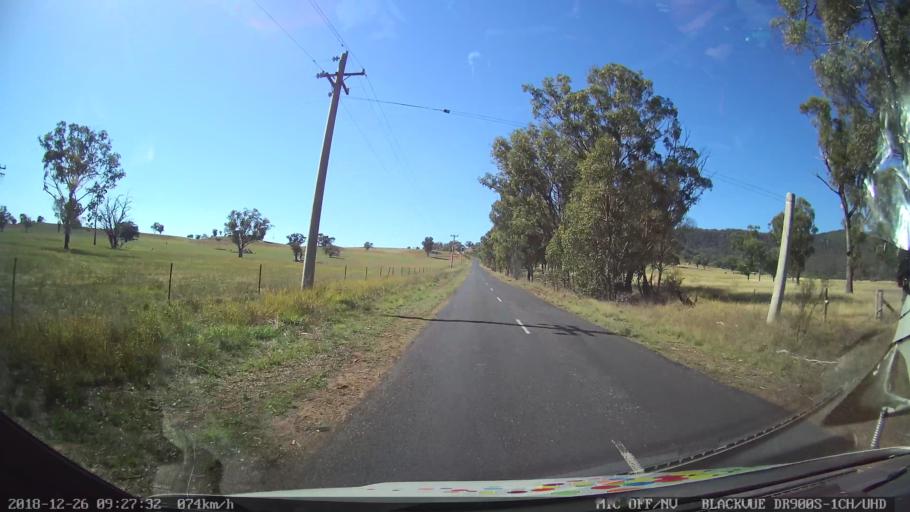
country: AU
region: New South Wales
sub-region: Mid-Western Regional
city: Kandos
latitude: -32.8367
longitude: 150.0174
